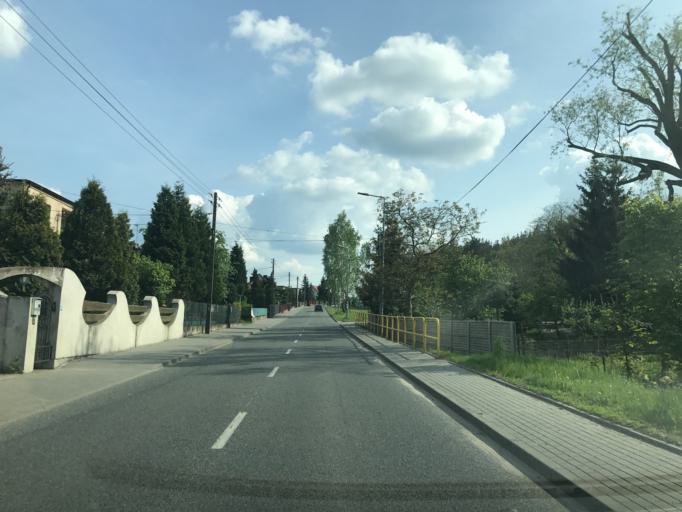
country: PL
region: Kujawsko-Pomorskie
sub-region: Bydgoszcz
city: Fordon
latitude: 53.1103
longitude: 18.1086
